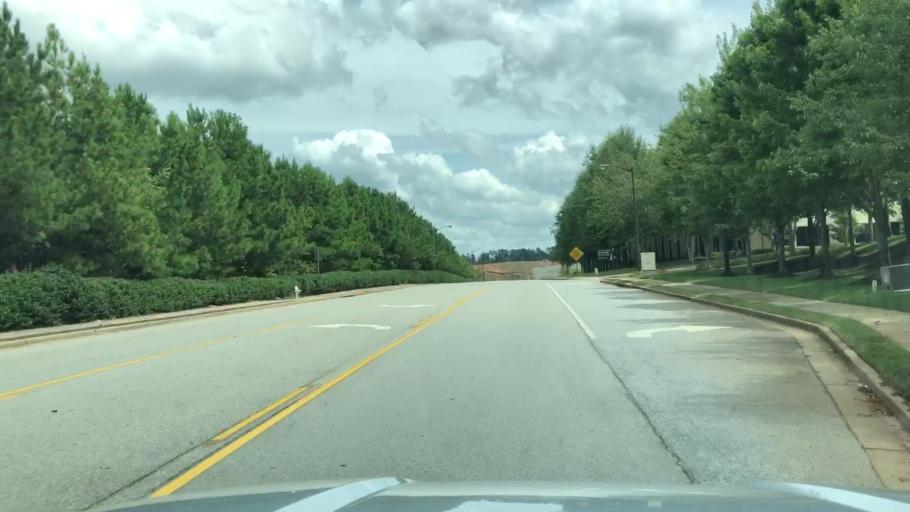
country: US
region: Georgia
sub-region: Gwinnett County
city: Suwanee
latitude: 34.0417
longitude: -84.0305
